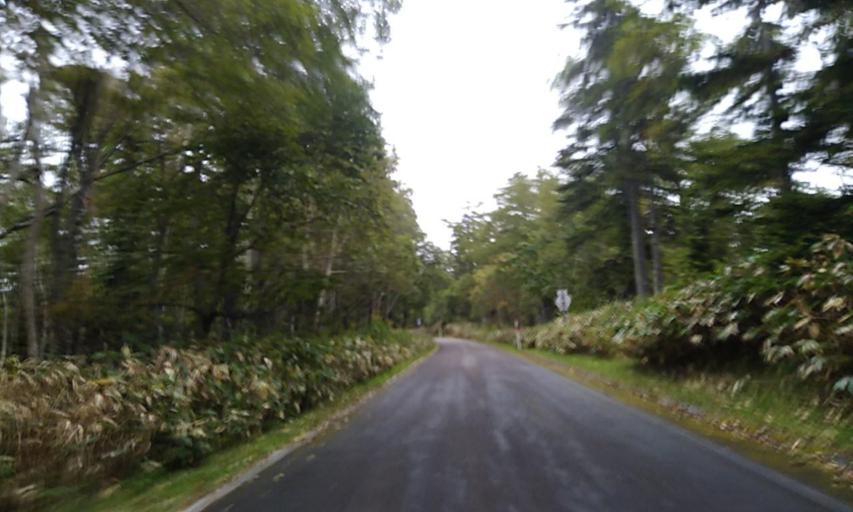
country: JP
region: Hokkaido
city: Bihoro
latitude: 43.5678
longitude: 144.2187
